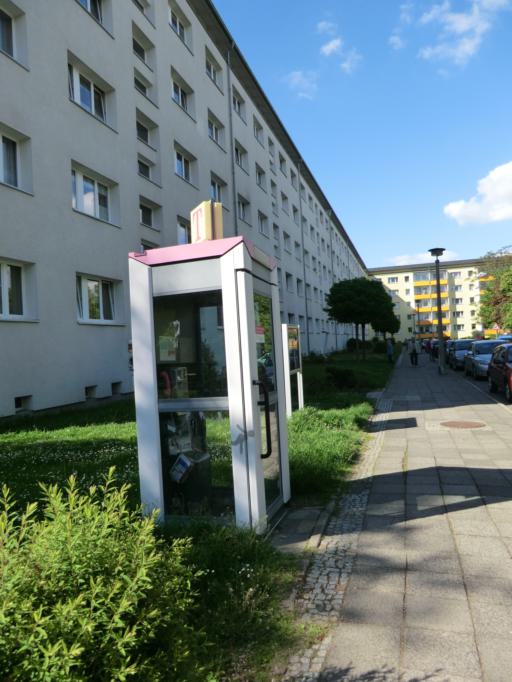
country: DE
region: Saxony
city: Goerlitz
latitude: 51.1249
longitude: 14.9731
